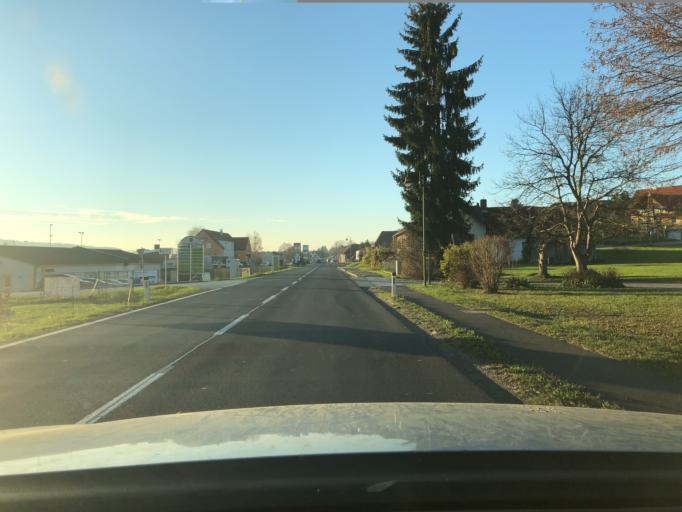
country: AT
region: Styria
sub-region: Politischer Bezirk Hartberg-Fuerstenfeld
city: Nestelbach im Ilztal
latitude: 47.0905
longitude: 15.8865
